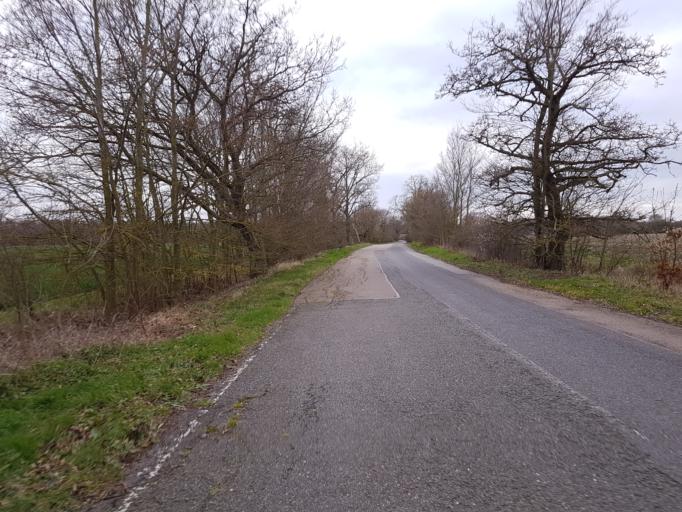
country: GB
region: England
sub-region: Cambridgeshire
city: Girton
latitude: 52.2317
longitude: 0.0490
